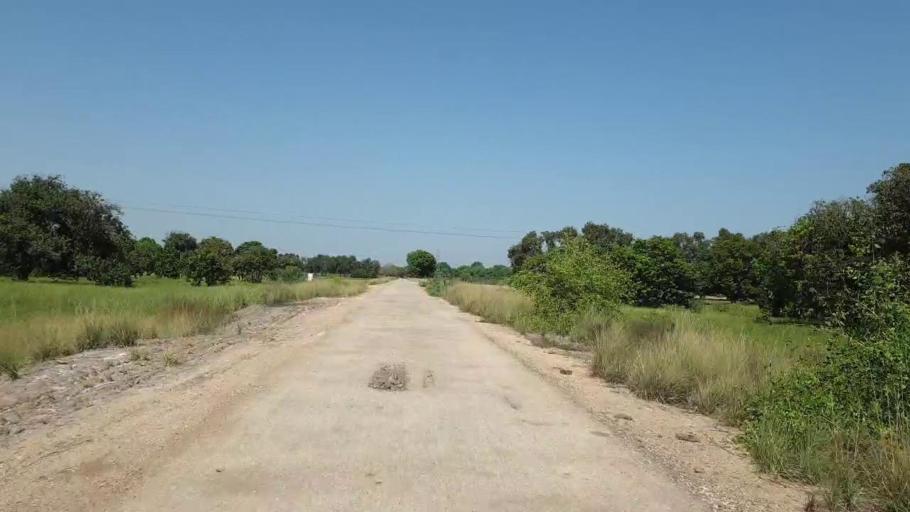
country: PK
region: Sindh
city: Tando Jam
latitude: 25.4238
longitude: 68.4588
